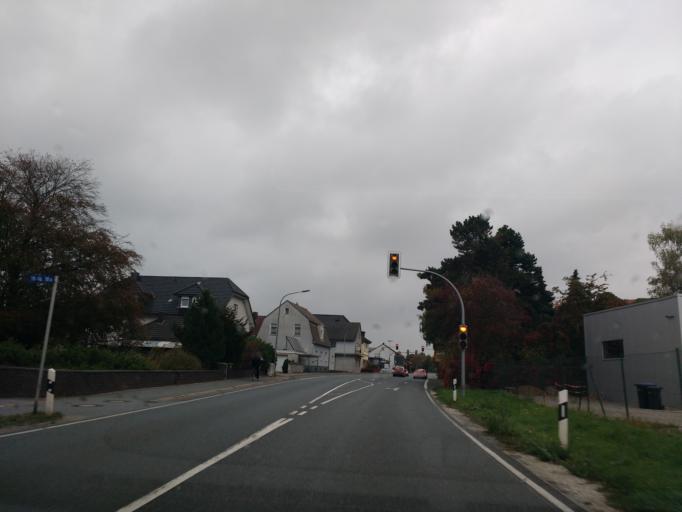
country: DE
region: North Rhine-Westphalia
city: Borgholzhausen
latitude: 52.0868
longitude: 8.2663
